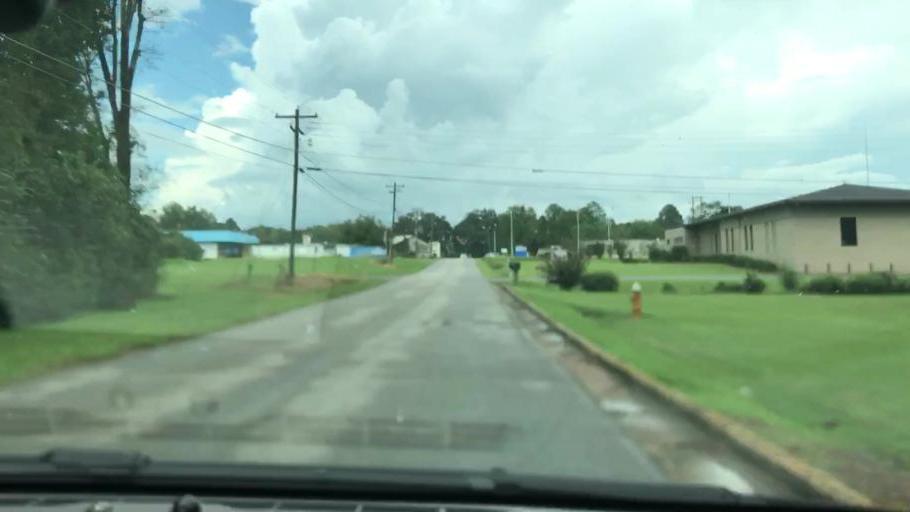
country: US
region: Georgia
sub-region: Early County
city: Blakely
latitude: 31.3704
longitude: -84.9470
